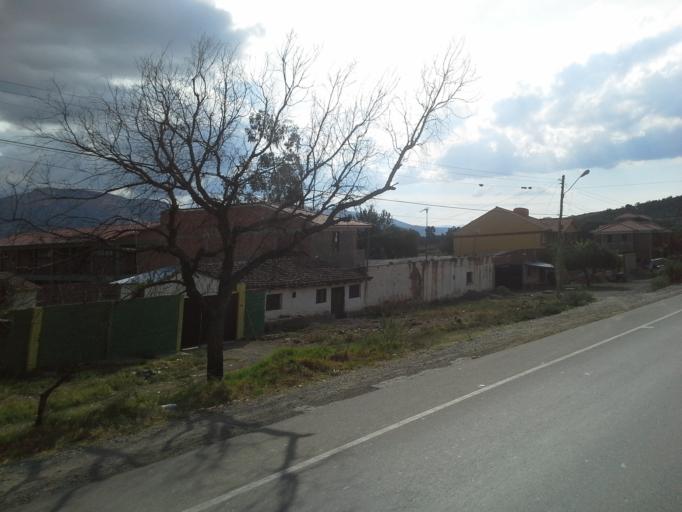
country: BO
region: Cochabamba
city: Tarata
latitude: -17.5421
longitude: -66.0336
